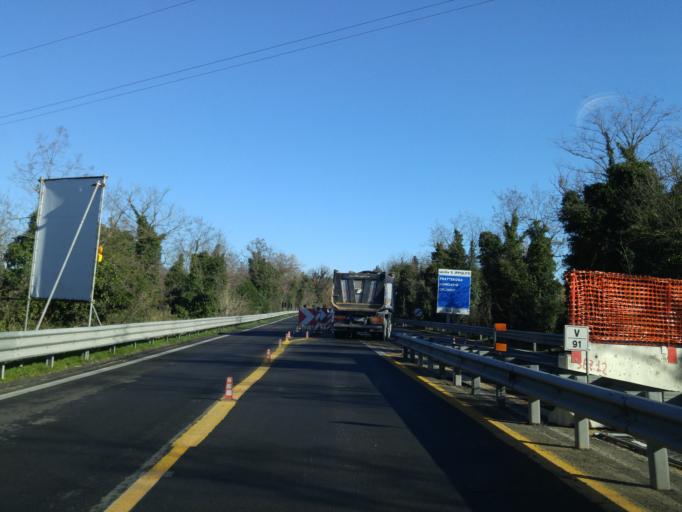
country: IT
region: The Marches
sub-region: Provincia di Pesaro e Urbino
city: Sant'Ippolito
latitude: 43.6988
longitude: 12.8640
